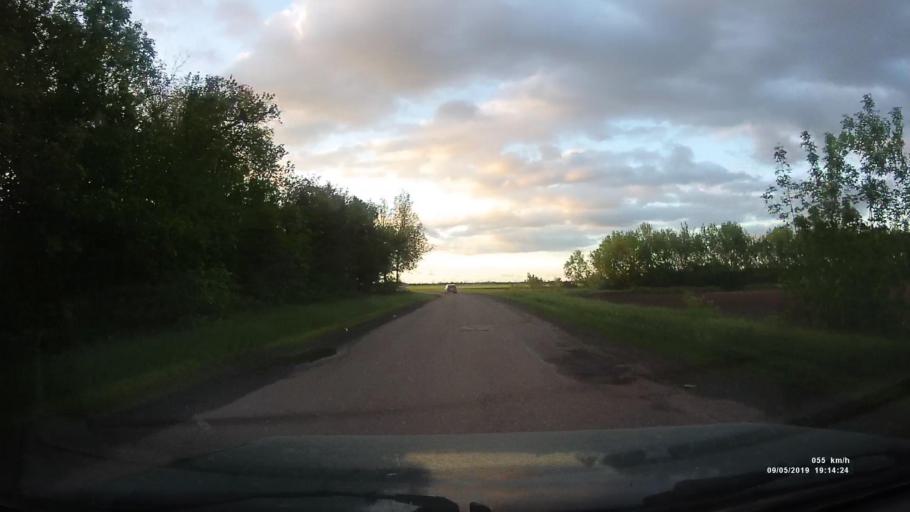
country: RU
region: Krasnodarskiy
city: Kanelovskaya
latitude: 46.7580
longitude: 39.2141
